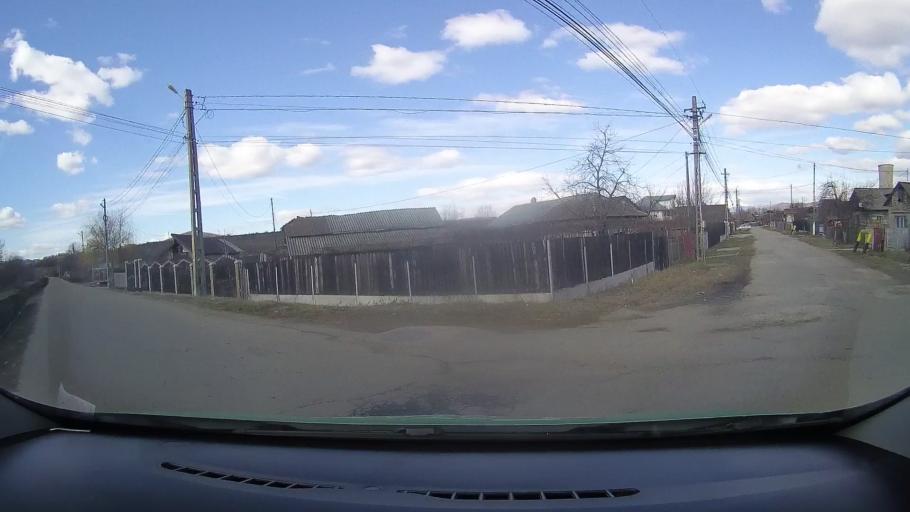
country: RO
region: Dambovita
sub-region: Comuna Doicesti
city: Doicesti
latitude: 44.9959
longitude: 25.3926
